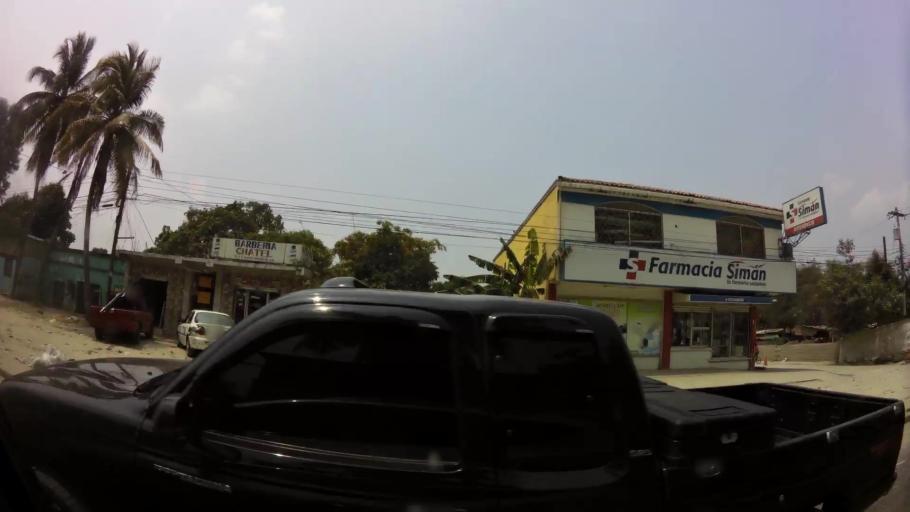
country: HN
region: Cortes
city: San Pedro Sula
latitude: 15.4776
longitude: -87.9856
